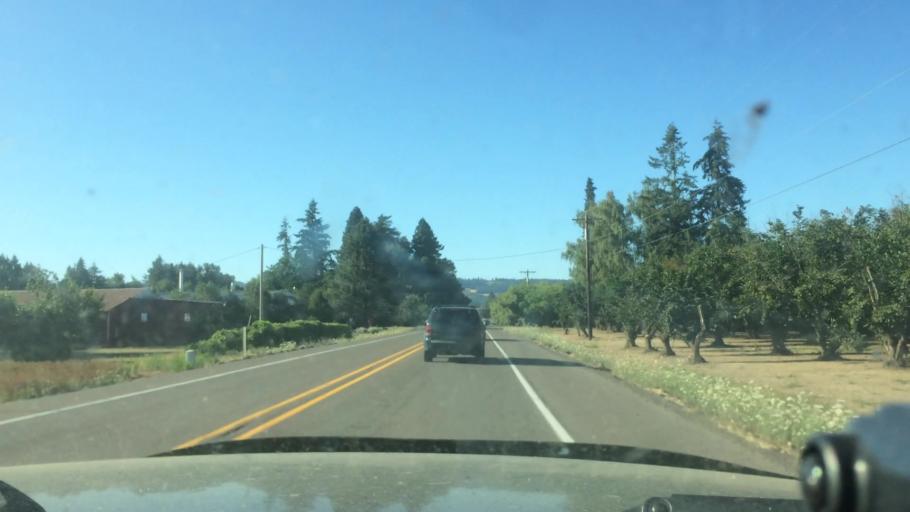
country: US
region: Oregon
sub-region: Yamhill County
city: Newberg
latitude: 45.2801
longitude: -122.9449
